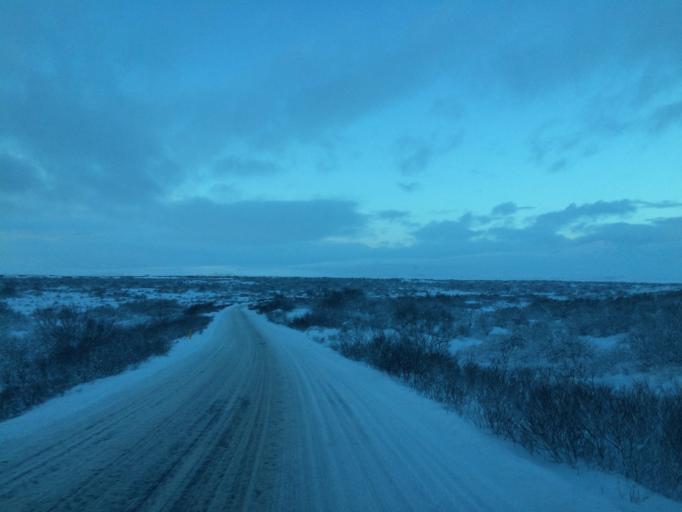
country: IS
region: South
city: Hveragerdi
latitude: 64.2601
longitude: -21.0399
